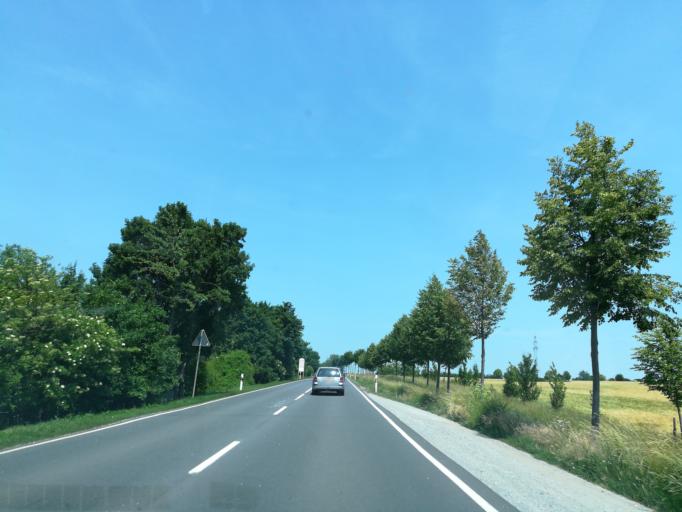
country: DE
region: Saxony-Anhalt
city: Aschersleben
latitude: 51.7760
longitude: 11.4570
